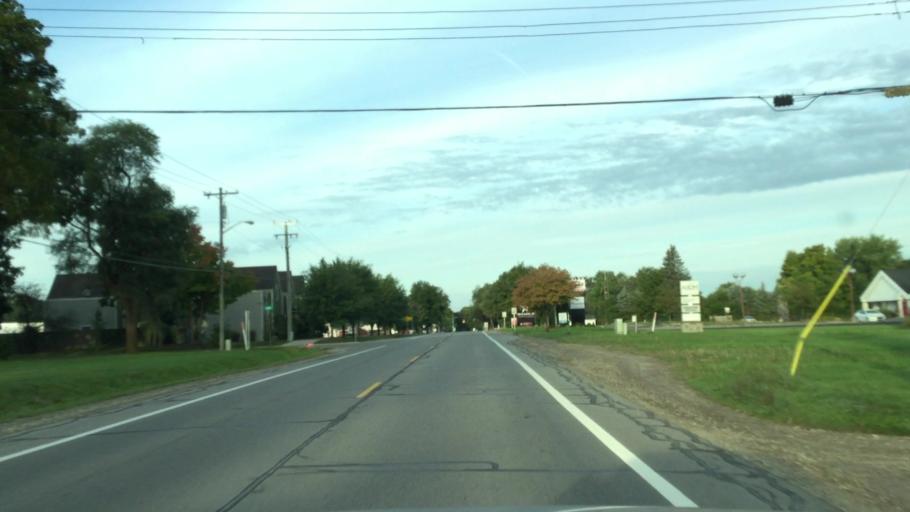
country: US
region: Michigan
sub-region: Livingston County
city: Whitmore Lake
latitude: 42.4523
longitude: -83.7928
